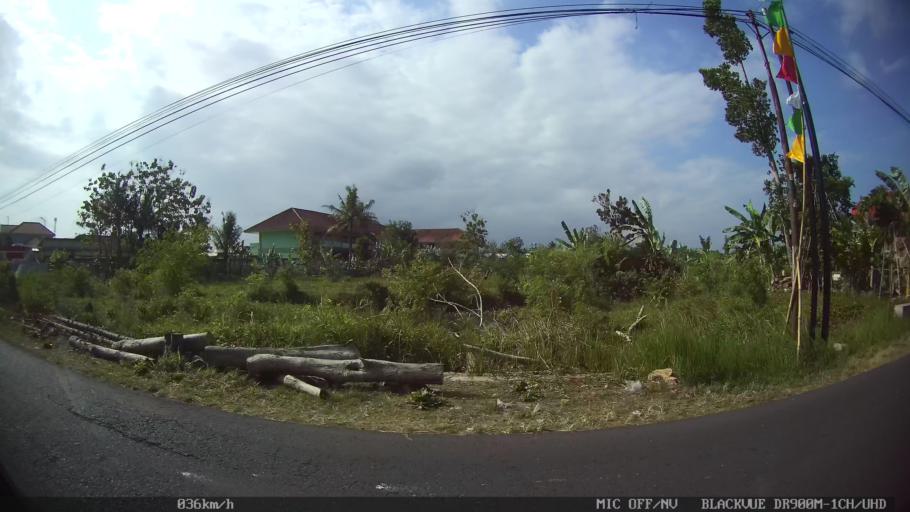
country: ID
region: Daerah Istimewa Yogyakarta
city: Sewon
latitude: -7.8729
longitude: 110.3669
